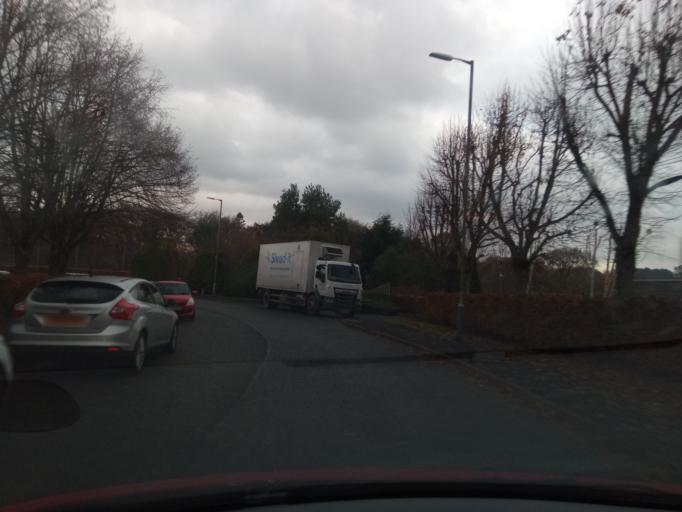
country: GB
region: Scotland
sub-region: The Scottish Borders
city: Melrose
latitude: 55.6040
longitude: -2.7518
